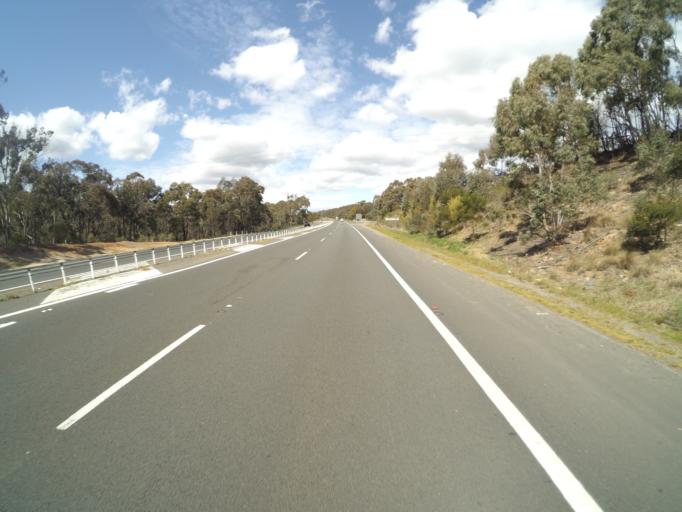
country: AU
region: New South Wales
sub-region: Goulburn Mulwaree
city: Goulburn
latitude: -34.7372
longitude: 149.8331
